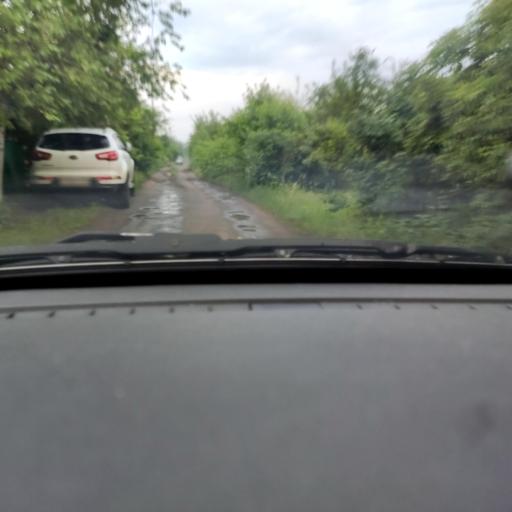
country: RU
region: Voronezj
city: Maslovka
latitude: 51.4928
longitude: 39.2141
